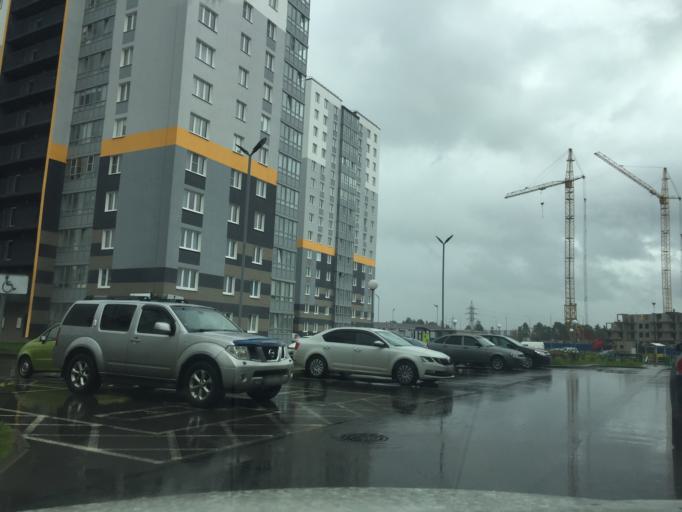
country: RU
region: St.-Petersburg
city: Gorelovo
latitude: 59.7888
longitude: 30.1648
